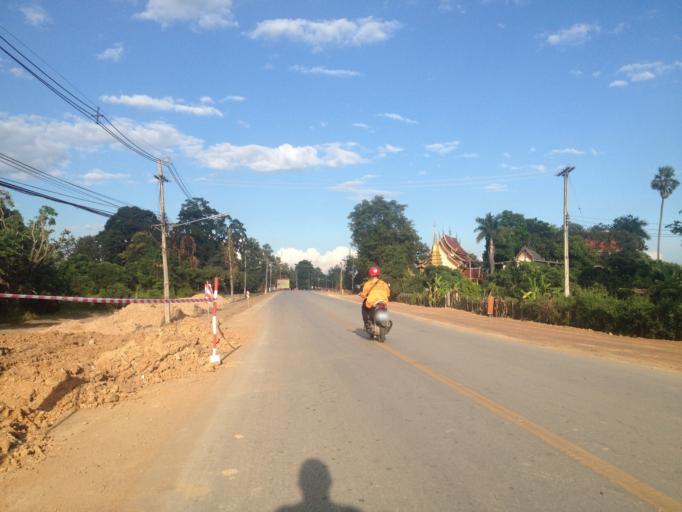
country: TH
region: Chiang Mai
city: San Pa Tong
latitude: 18.6092
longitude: 98.8423
